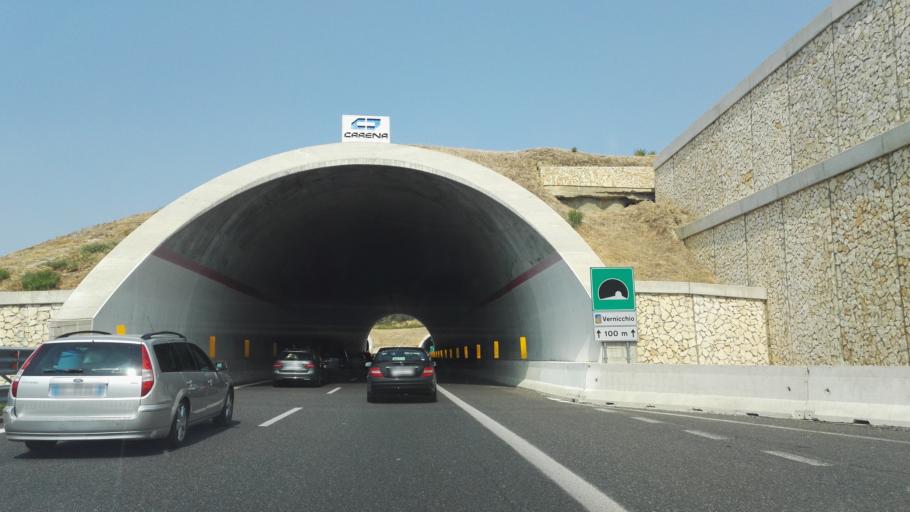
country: IT
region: Calabria
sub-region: Provincia di Cosenza
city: Tarsia
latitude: 39.6000
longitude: 16.2391
